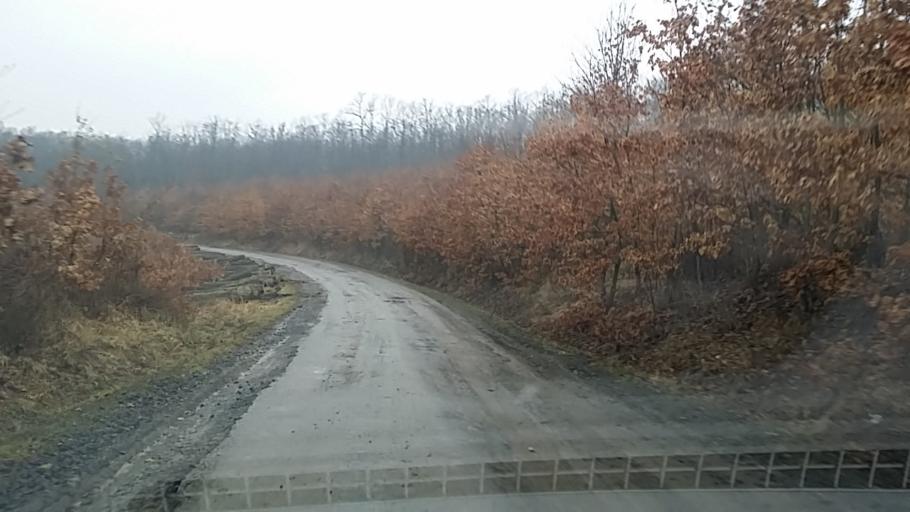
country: HU
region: Borsod-Abauj-Zemplen
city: Rudabanya
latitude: 48.4179
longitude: 20.5792
